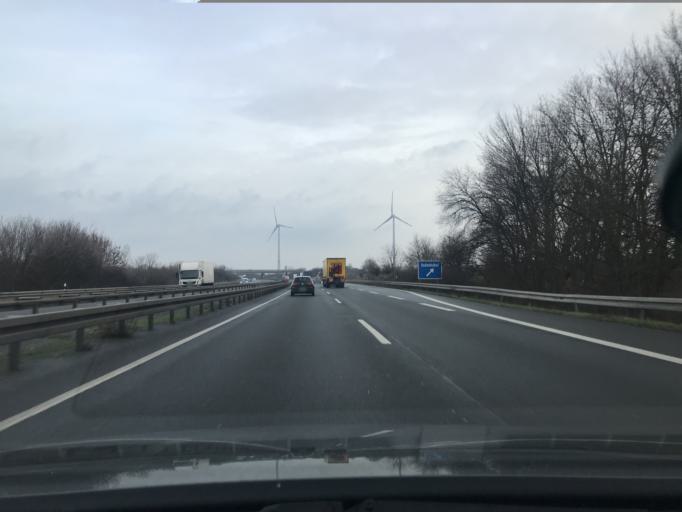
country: DE
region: North Rhine-Westphalia
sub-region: Regierungsbezirk Dusseldorf
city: Kamp-Lintfort
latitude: 51.5088
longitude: 6.5824
